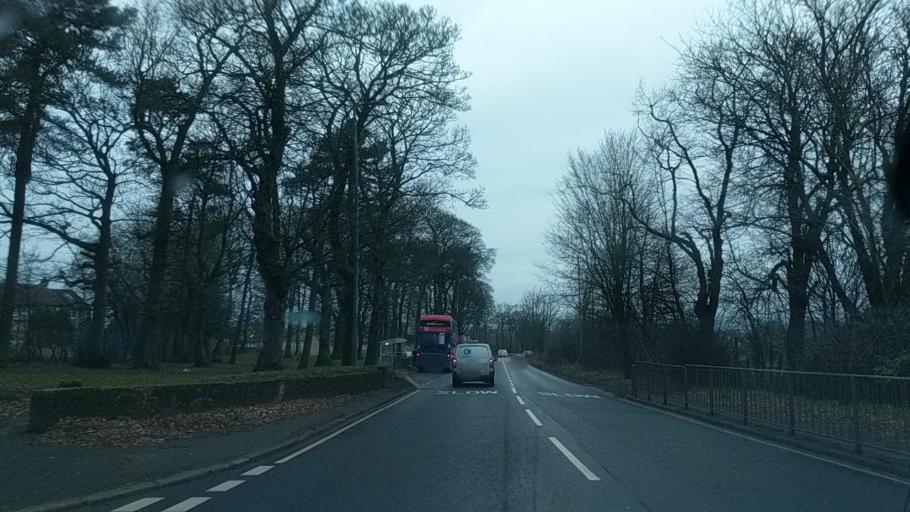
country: GB
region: Scotland
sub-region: South Lanarkshire
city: Rutherglen
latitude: 55.8042
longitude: -4.1831
